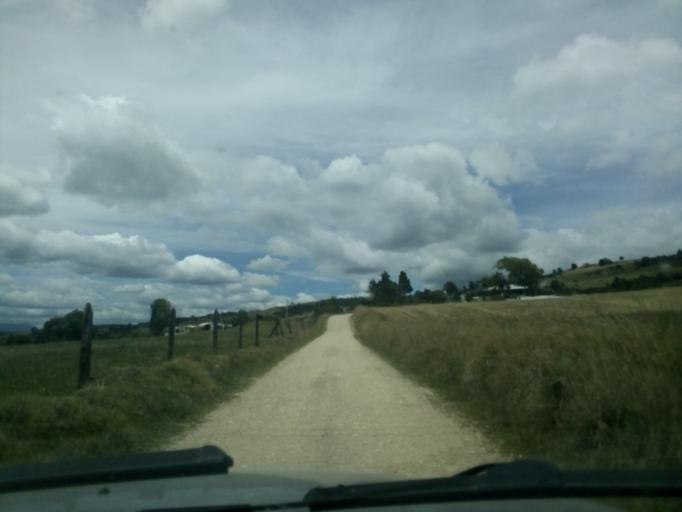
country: CO
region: Boyaca
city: Toca
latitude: 5.6228
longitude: -73.1298
